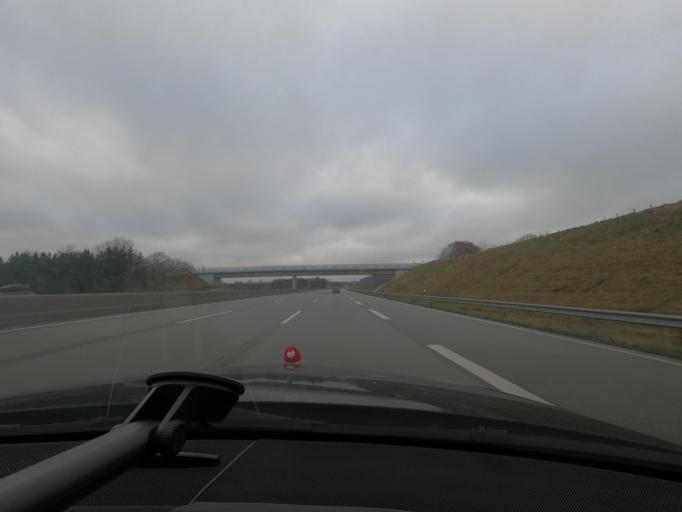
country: DE
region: Schleswig-Holstein
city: Bimohlen
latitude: 53.9073
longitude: 9.9368
